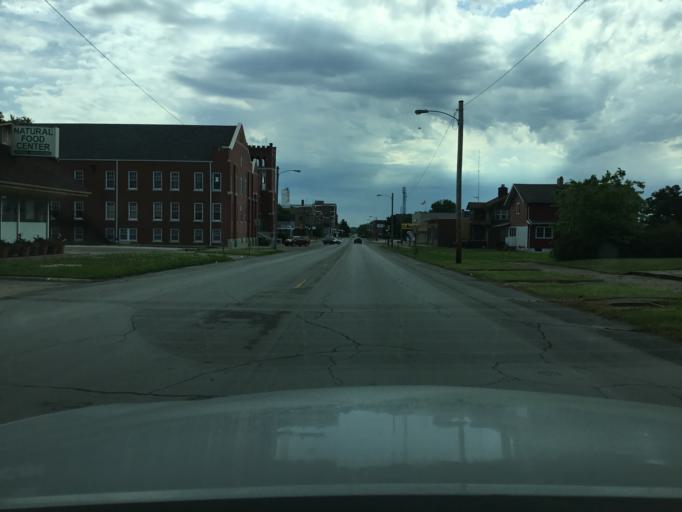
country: US
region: Kansas
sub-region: Montgomery County
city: Coffeyville
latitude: 37.0361
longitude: -95.6222
